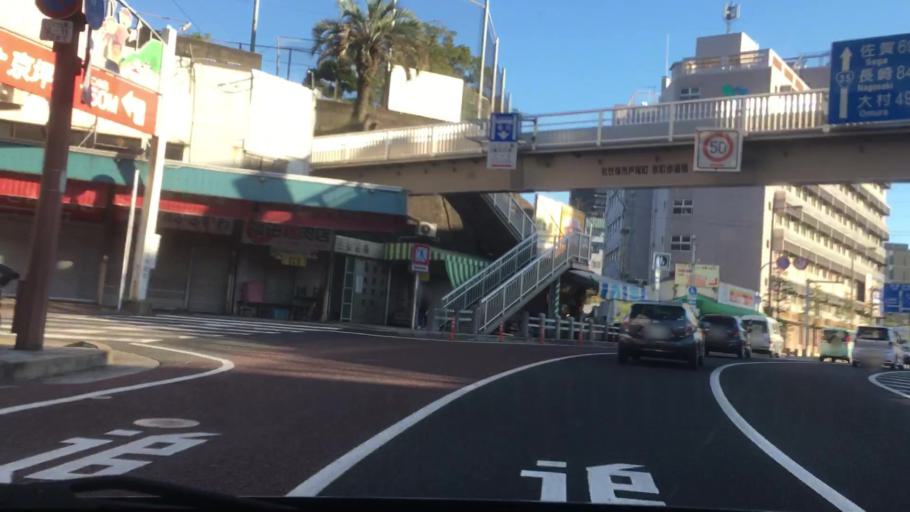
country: JP
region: Nagasaki
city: Sasebo
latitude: 33.1690
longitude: 129.7240
